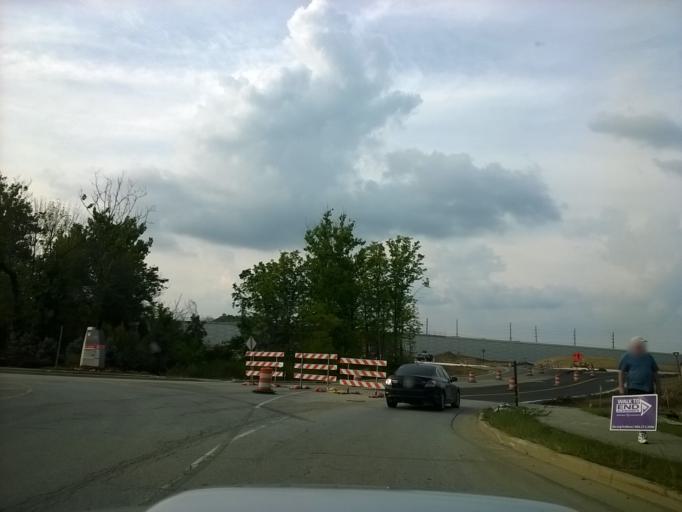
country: US
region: Indiana
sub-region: Hamilton County
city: Carmel
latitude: 39.9826
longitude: -86.1413
